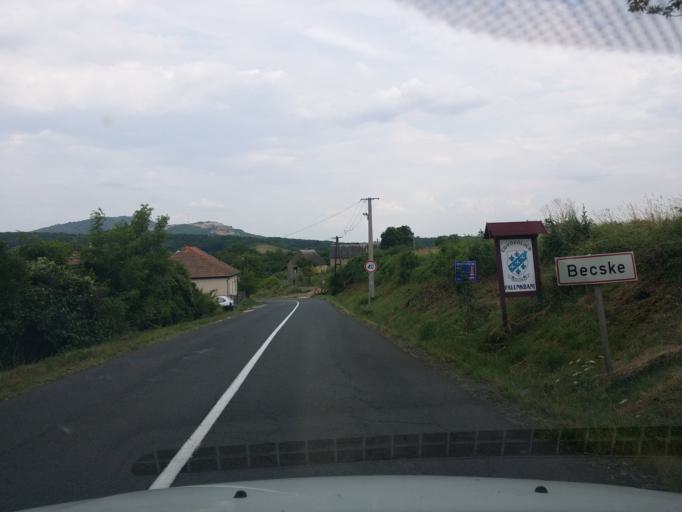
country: HU
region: Nograd
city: Bercel
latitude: 47.9148
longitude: 19.3720
